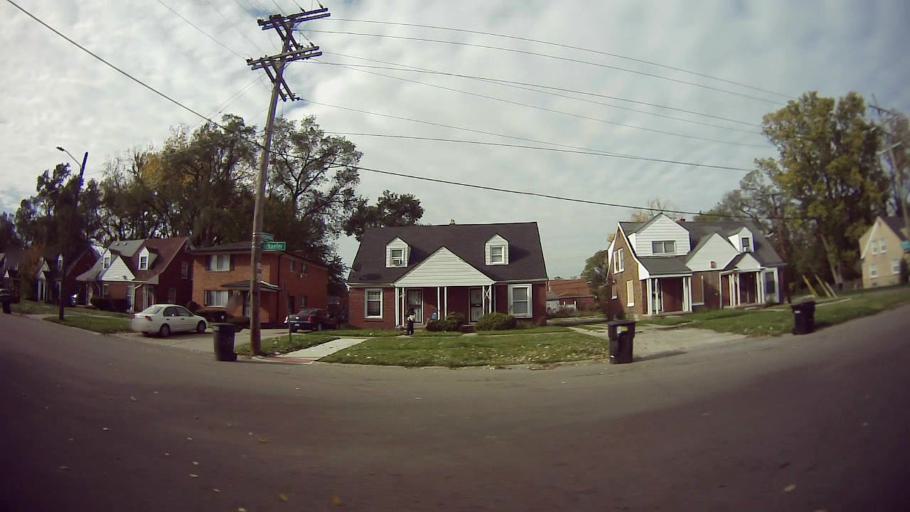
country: US
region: Michigan
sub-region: Oakland County
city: Oak Park
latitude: 42.4405
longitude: -83.1808
